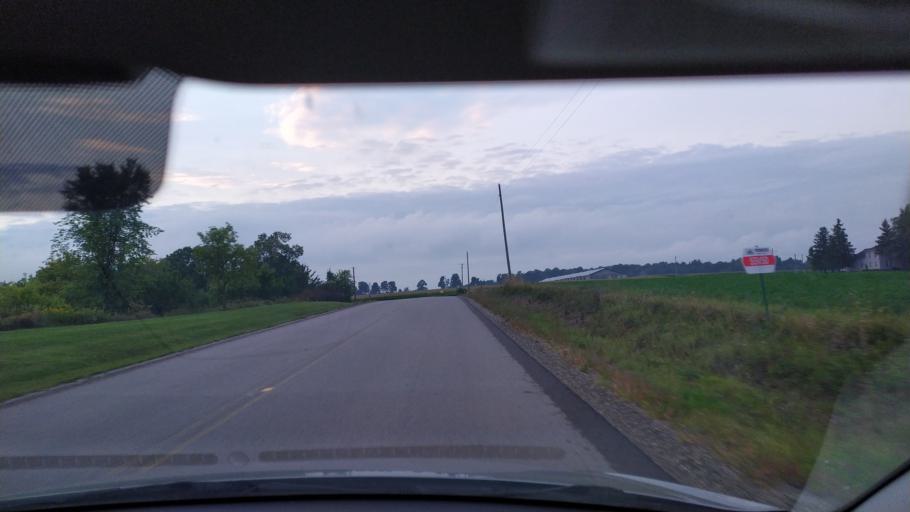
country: CA
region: Ontario
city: Kitchener
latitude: 43.3452
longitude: -80.6367
